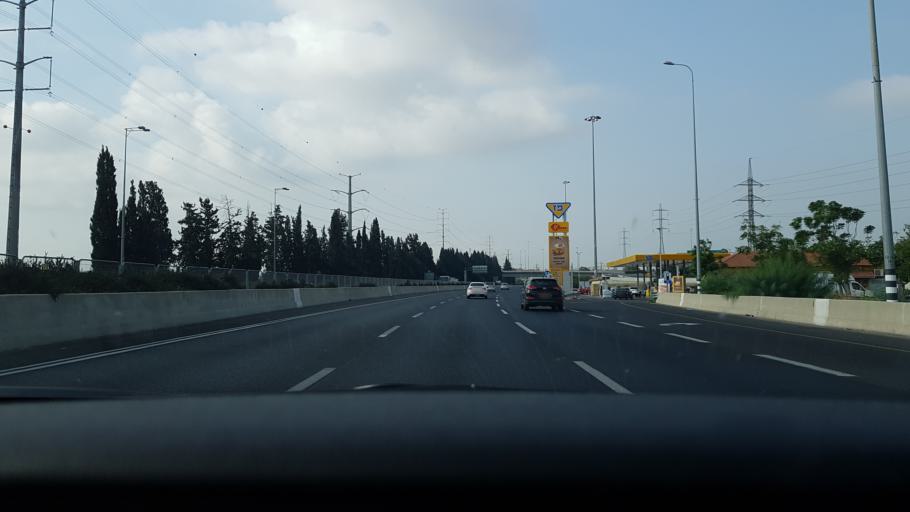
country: IL
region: Central District
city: Bet Dagan
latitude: 32.0032
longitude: 34.8089
